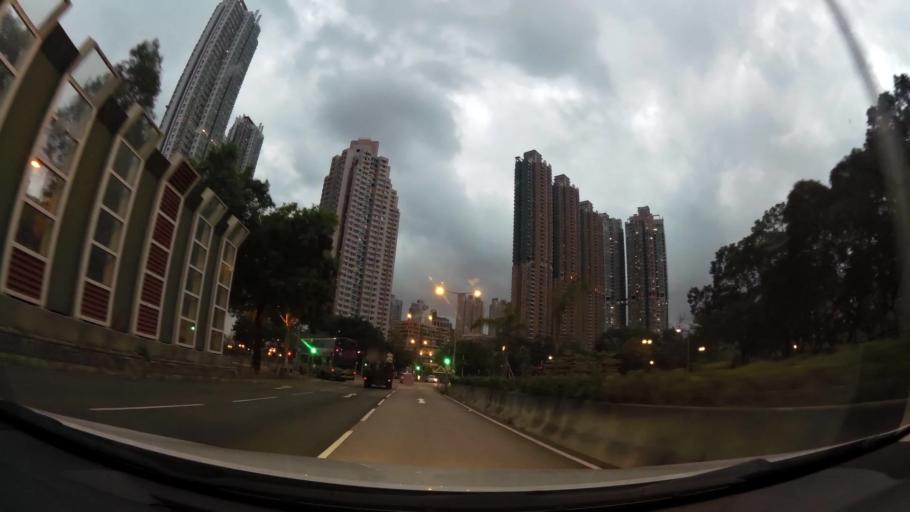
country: HK
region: Sham Shui Po
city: Sham Shui Po
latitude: 22.3248
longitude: 114.1577
